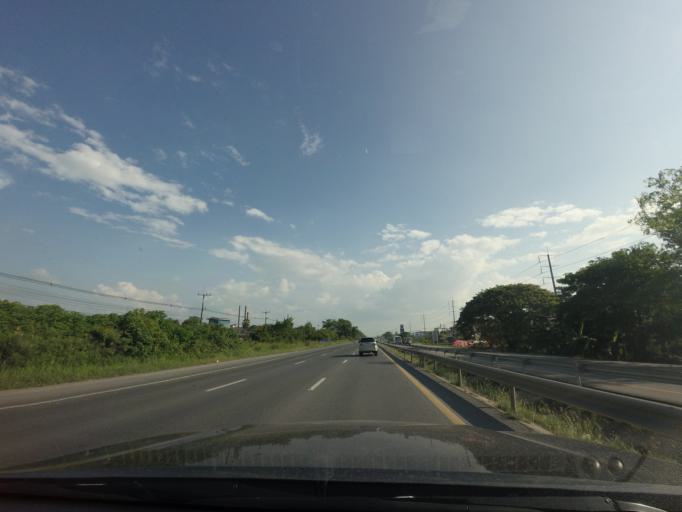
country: TH
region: Sara Buri
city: Chaloem Phra Kiat
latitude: 14.6393
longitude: 100.8871
